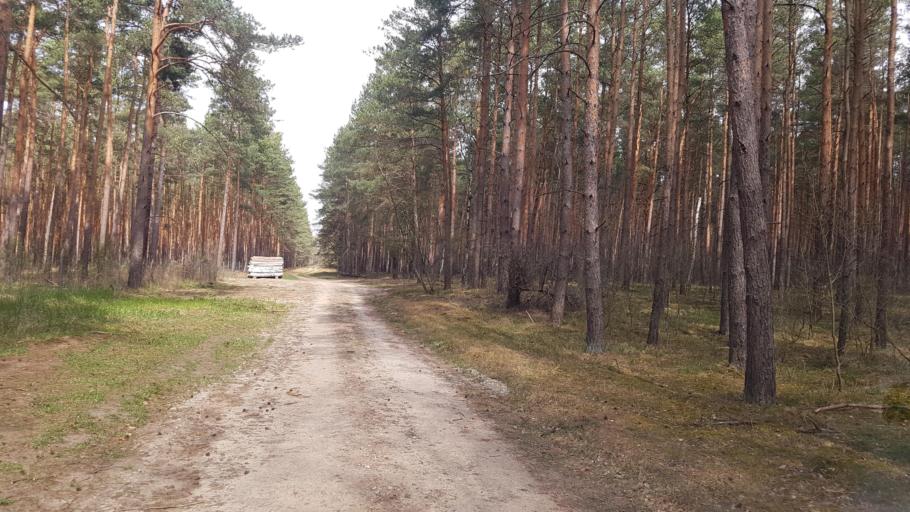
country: DE
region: Brandenburg
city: Luckenwalde
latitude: 52.1378
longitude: 13.1718
